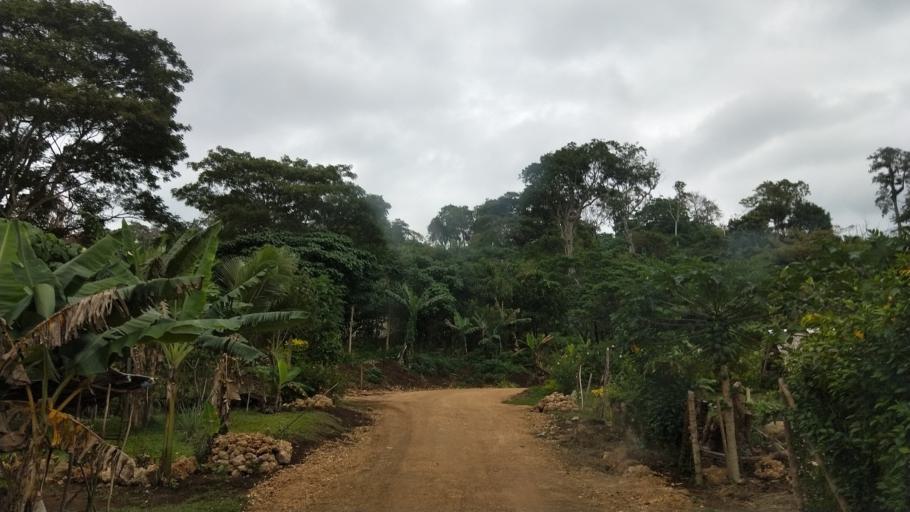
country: VU
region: Sanma
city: Luganville
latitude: -15.5352
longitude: 167.1490
